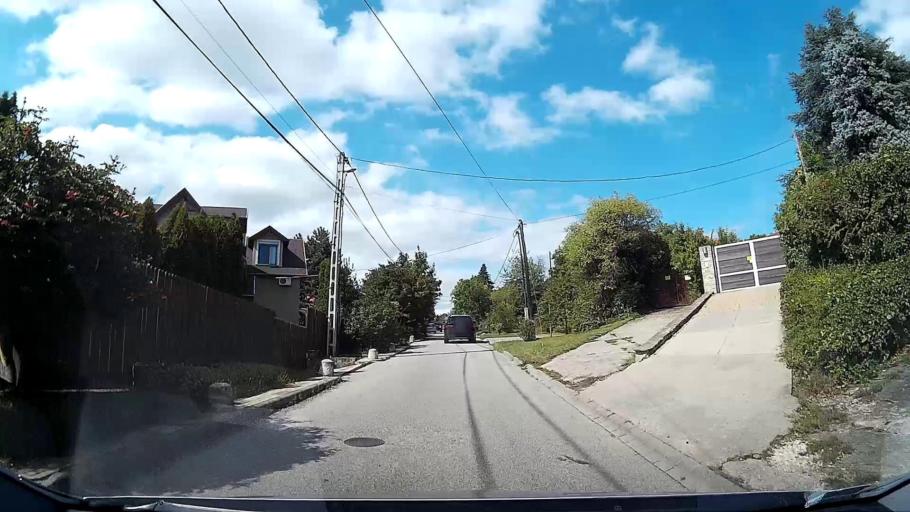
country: HU
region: Pest
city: Szentendre
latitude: 47.6866
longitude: 19.0738
